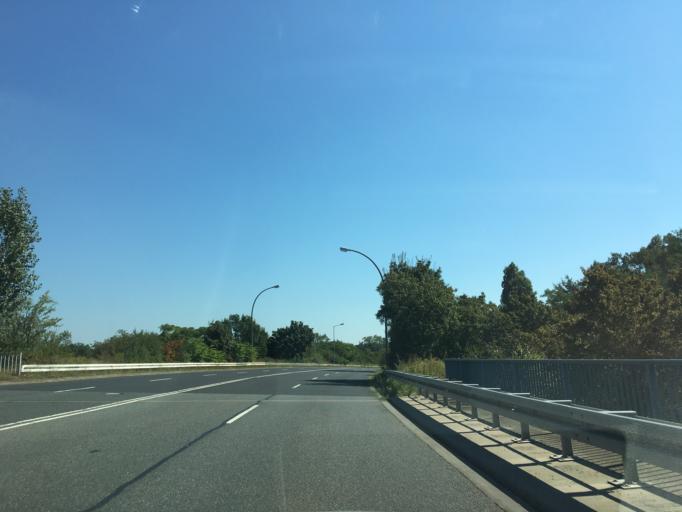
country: DE
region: Hesse
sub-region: Regierungsbezirk Darmstadt
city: Russelsheim
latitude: 49.9784
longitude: 8.4131
